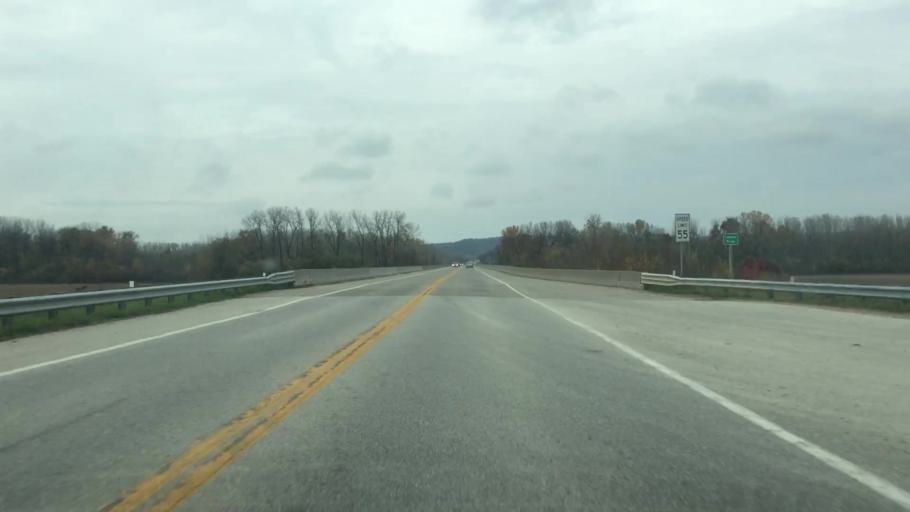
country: US
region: Missouri
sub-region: Gasconade County
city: Hermann
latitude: 38.7147
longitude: -91.4408
